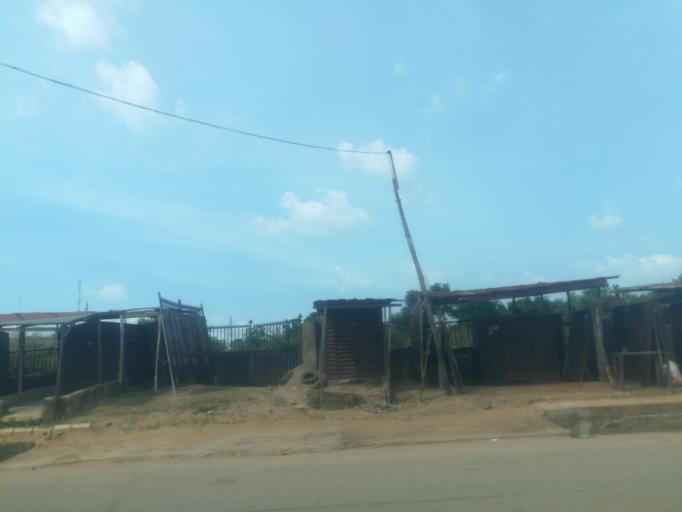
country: NG
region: Ogun
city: Abeokuta
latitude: 7.1625
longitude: 3.3736
